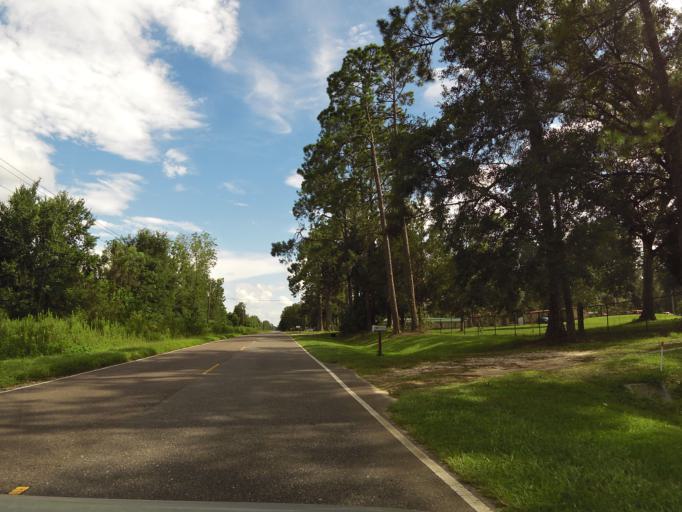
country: US
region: Florida
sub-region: Clay County
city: Green Cove Springs
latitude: 29.9640
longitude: -81.6934
